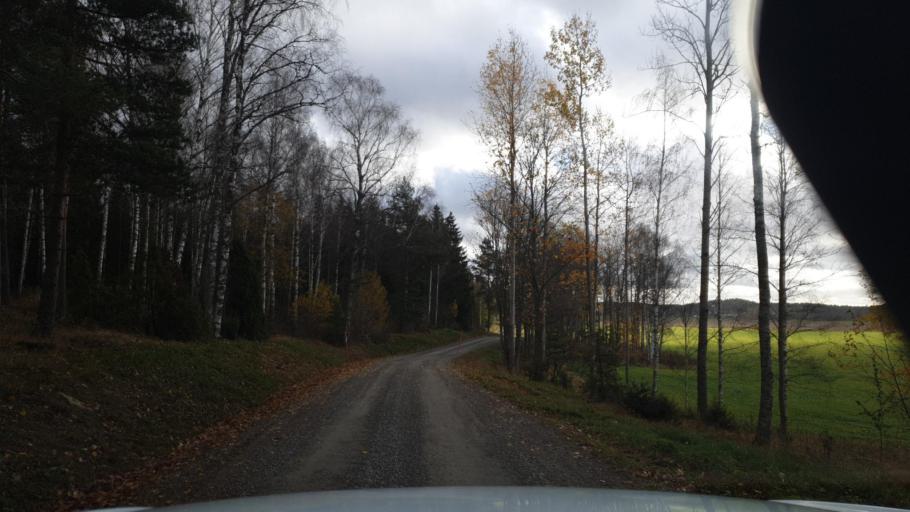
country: SE
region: Vaermland
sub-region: Arvika Kommun
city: Arvika
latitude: 59.4959
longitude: 12.7324
